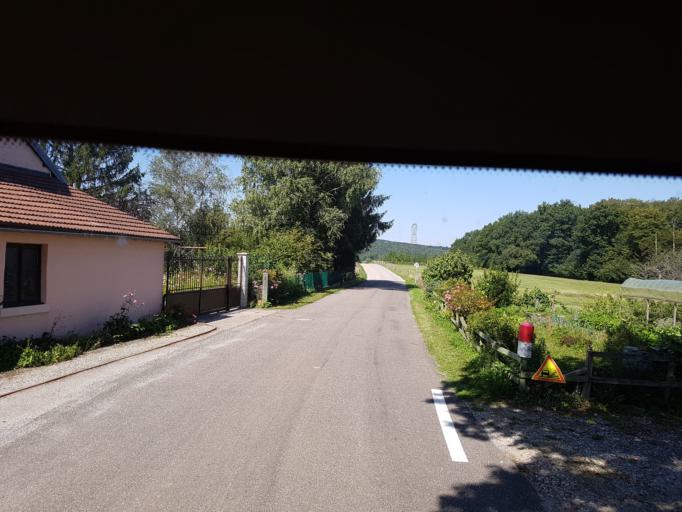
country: FR
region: Franche-Comte
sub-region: Departement du Jura
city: Perrigny
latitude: 46.7326
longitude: 5.5722
